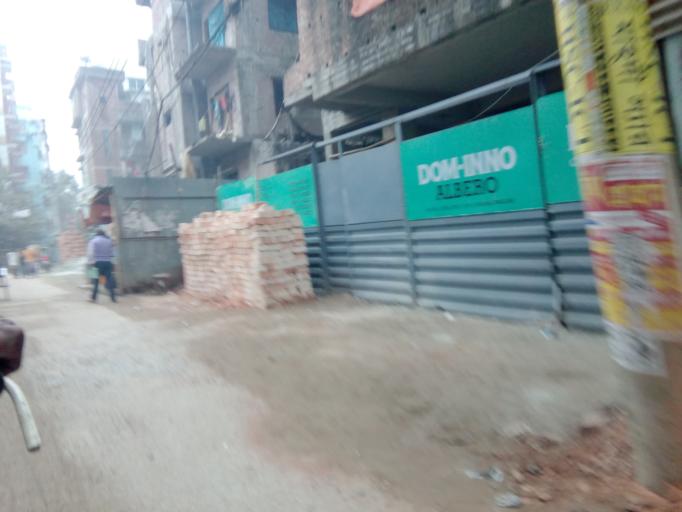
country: BD
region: Dhaka
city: Paltan
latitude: 23.7465
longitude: 90.4166
